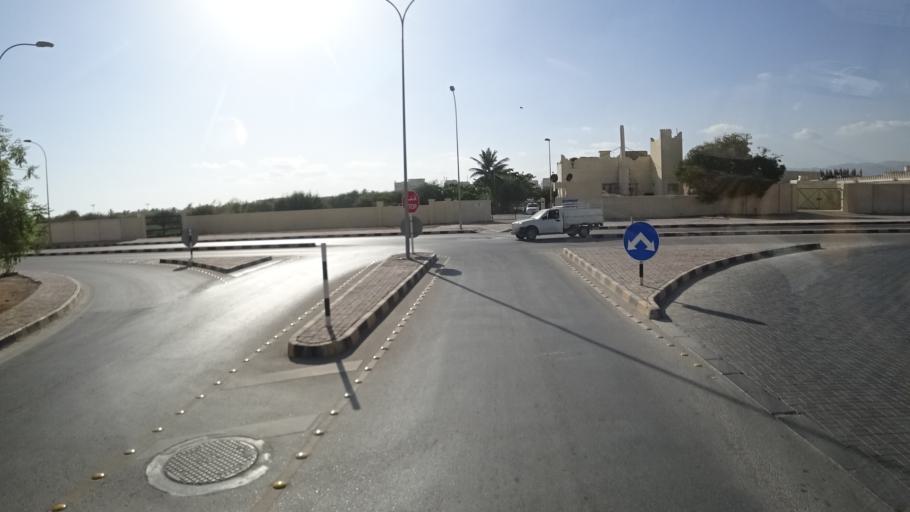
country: OM
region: Zufar
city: Salalah
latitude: 17.0049
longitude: 54.0689
